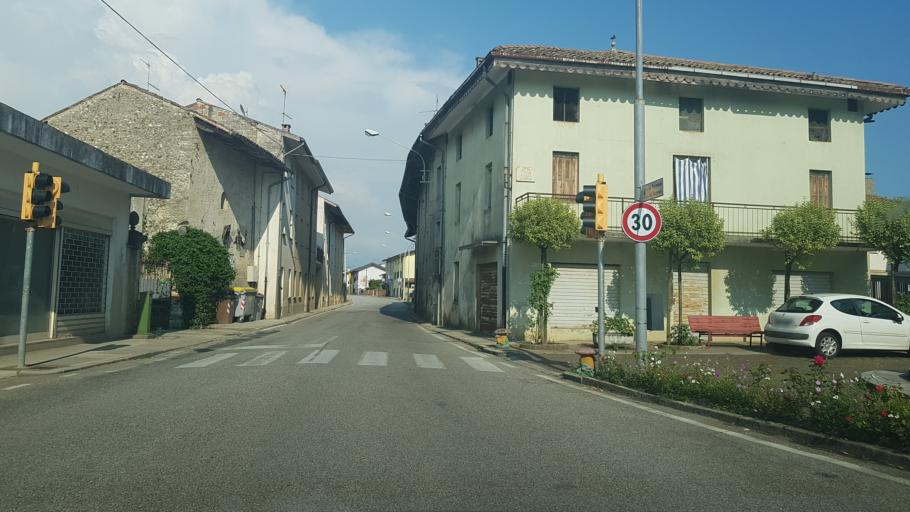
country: IT
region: Friuli Venezia Giulia
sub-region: Provincia di Udine
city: Basiliano-Vissandone
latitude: 46.0570
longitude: 13.0856
